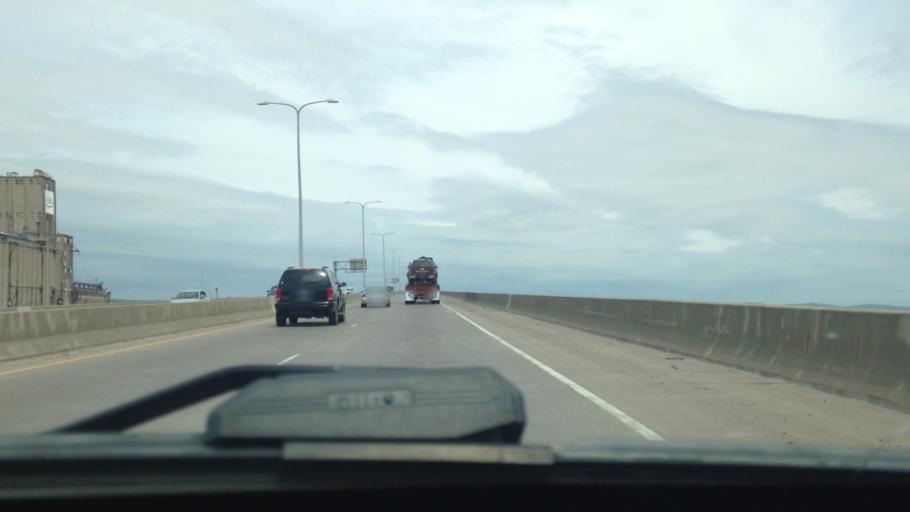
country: US
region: Wisconsin
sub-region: Douglas County
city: Superior
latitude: 46.7370
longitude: -92.0977
